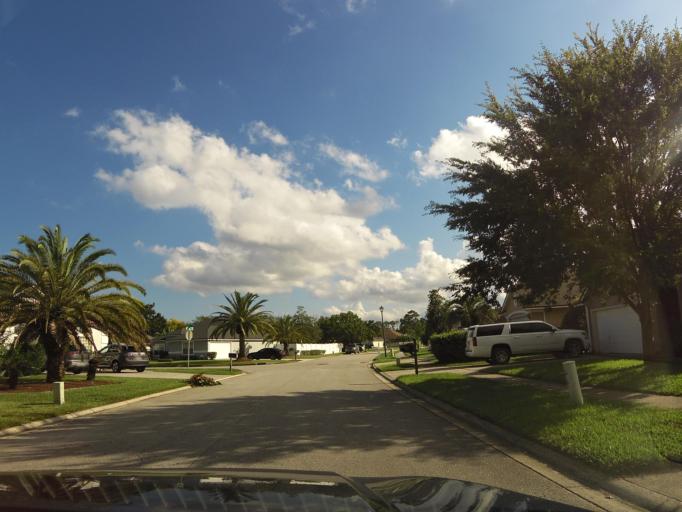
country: US
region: Florida
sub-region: Duval County
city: Jacksonville Beach
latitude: 30.2767
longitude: -81.4969
